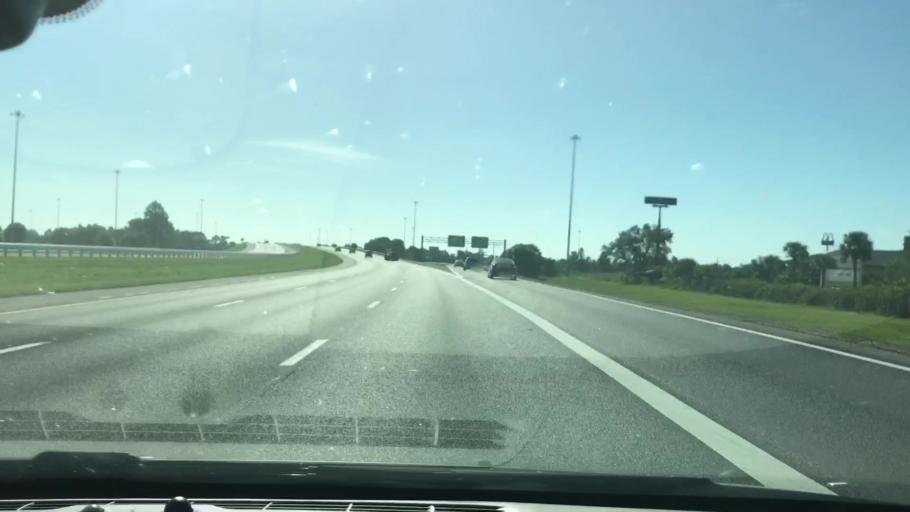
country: US
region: Florida
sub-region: Charlotte County
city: Charlotte Park
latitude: 26.8992
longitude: -82.0066
